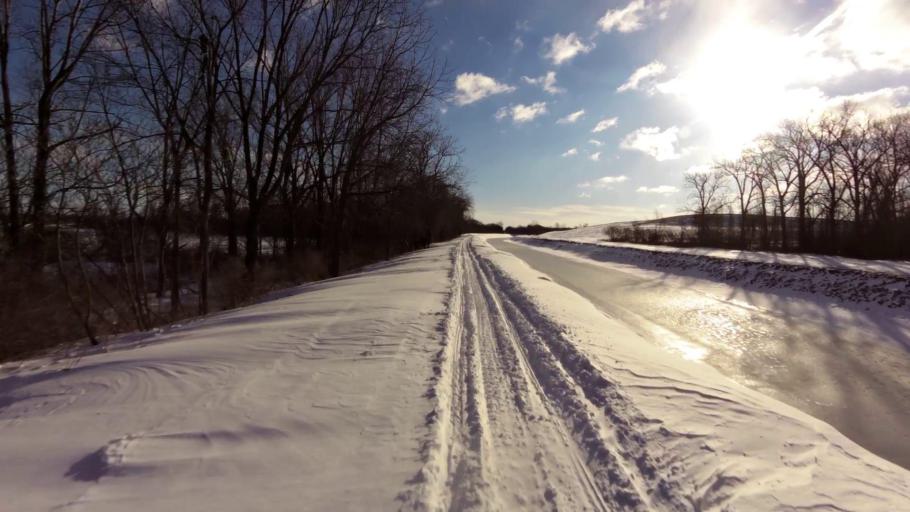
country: US
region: New York
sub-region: Orleans County
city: Albion
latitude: 43.2510
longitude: -78.1261
